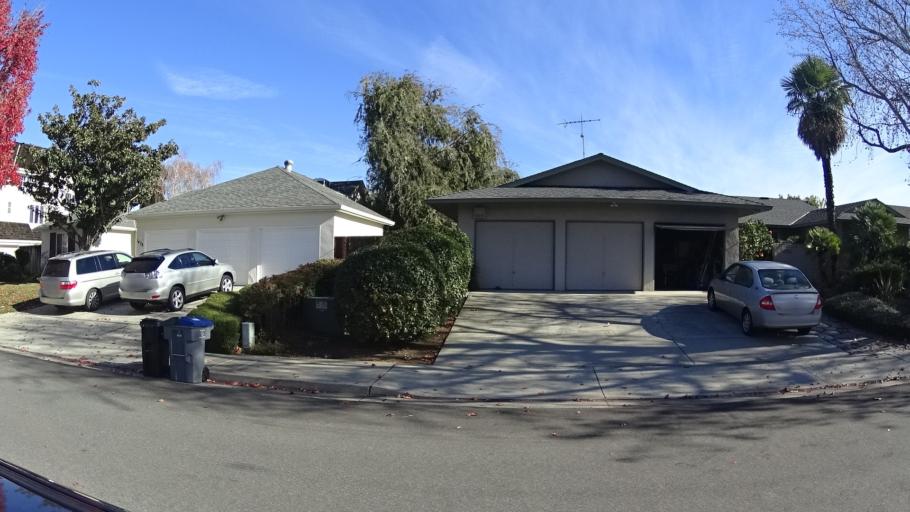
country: US
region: California
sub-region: Santa Clara County
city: Cupertino
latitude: 37.3451
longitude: -122.0346
